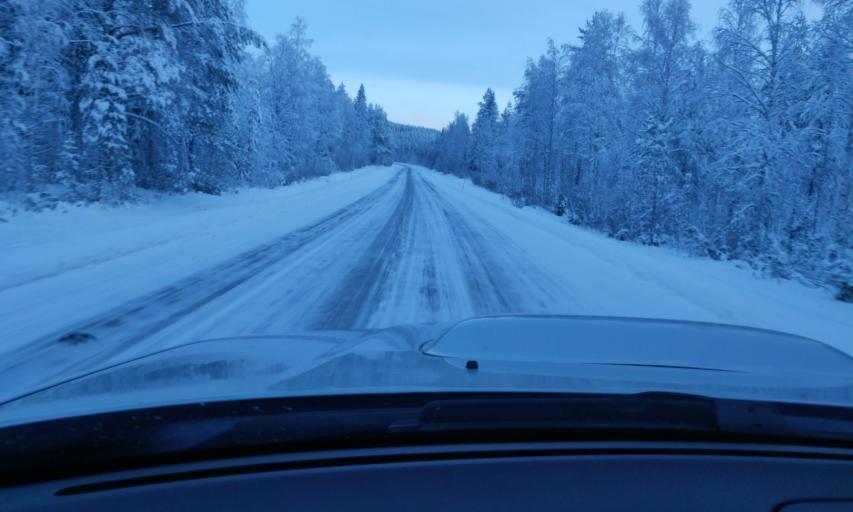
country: FI
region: Kainuu
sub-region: Kehys-Kainuu
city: Suomussalmi
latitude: 64.9010
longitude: 29.0333
